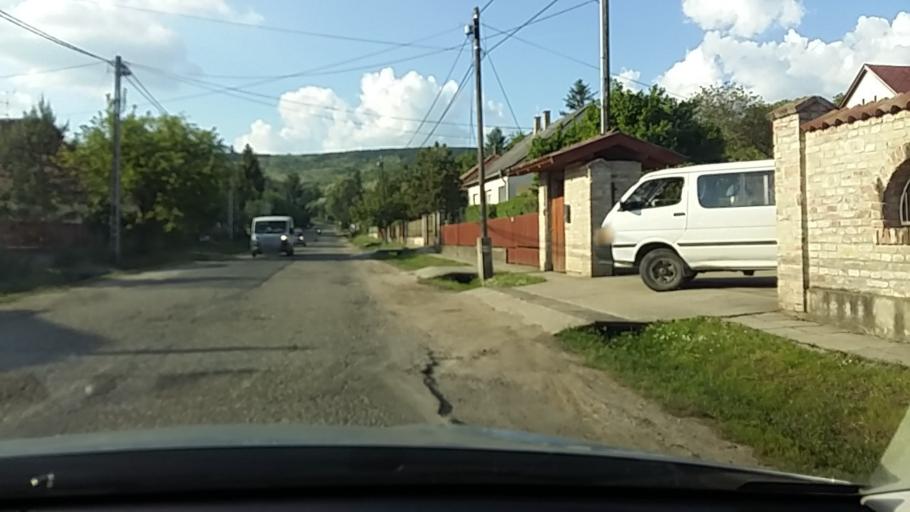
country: HU
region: Pest
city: Kosd
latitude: 47.8076
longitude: 19.2506
